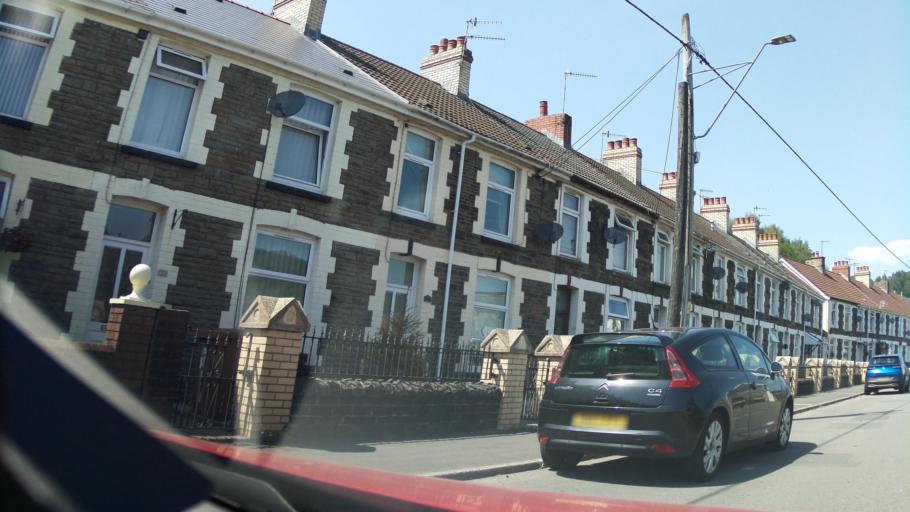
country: GB
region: Wales
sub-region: Caerphilly County Borough
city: Llanbradach
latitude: 51.6114
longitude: -3.2275
